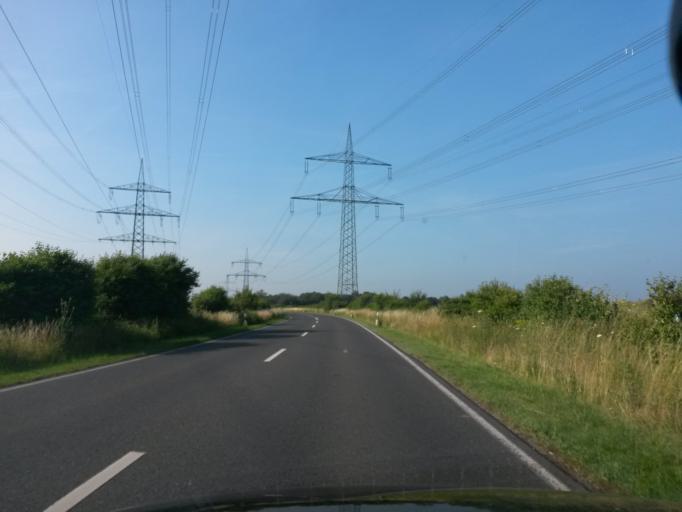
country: DE
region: North Rhine-Westphalia
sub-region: Regierungsbezirk Koln
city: Alfter
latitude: 50.7310
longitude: 7.0332
